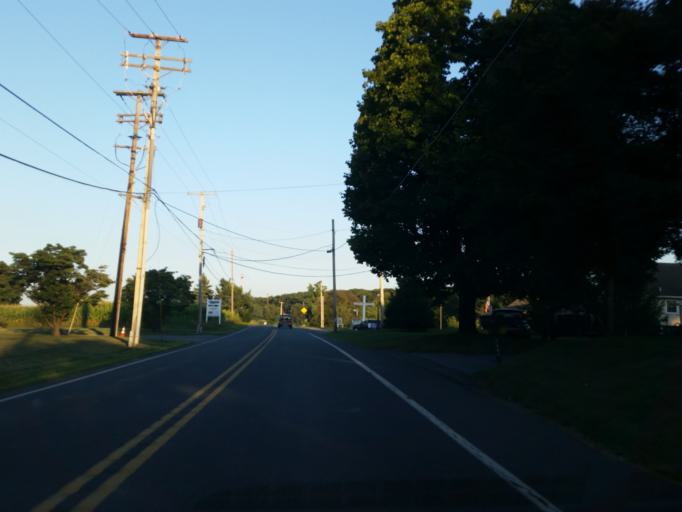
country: US
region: Pennsylvania
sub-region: Lebanon County
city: Sand Hill
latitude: 40.3745
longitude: -76.4373
